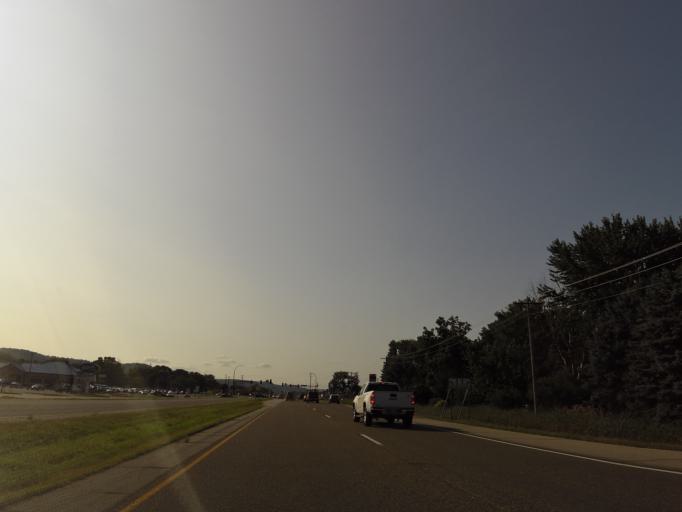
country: US
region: Minnesota
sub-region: Winona County
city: Goodview
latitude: 44.0469
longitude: -91.6744
